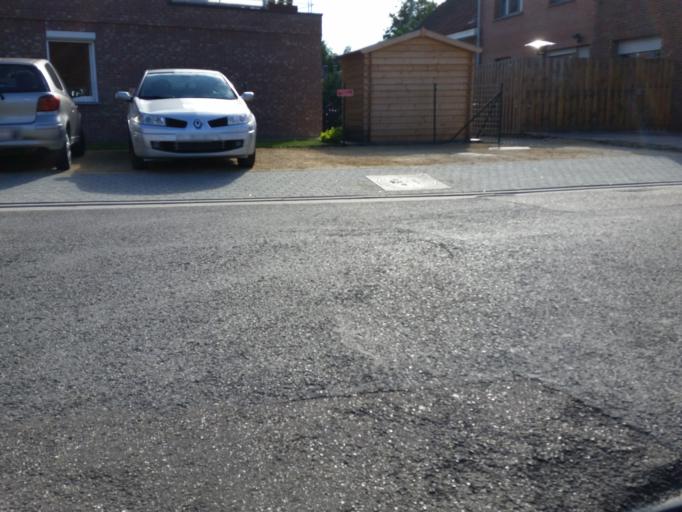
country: BE
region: Flanders
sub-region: Provincie Antwerpen
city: Mechelen
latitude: 51.0424
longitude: 4.4465
